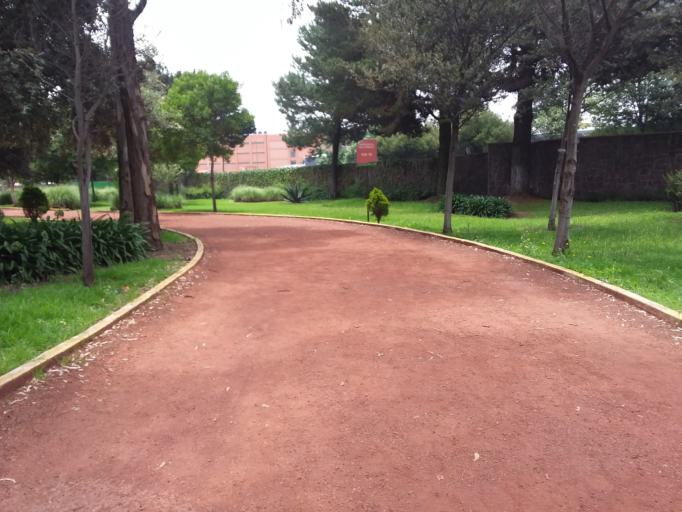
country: MX
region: Mexico
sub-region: Metepec
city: San Jorge Pueblo Nuevo
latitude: 19.2632
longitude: -99.6313
